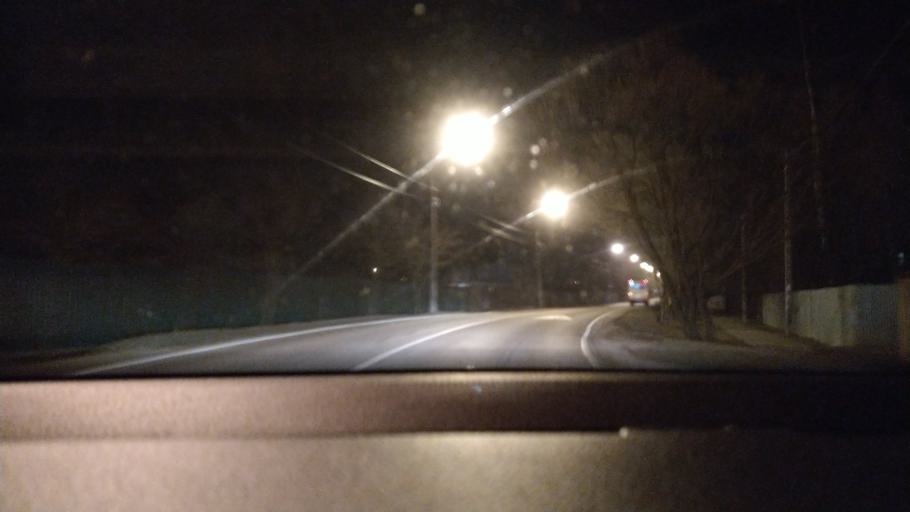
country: RU
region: Moskovskaya
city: Selyatino
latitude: 55.4805
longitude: 36.9213
